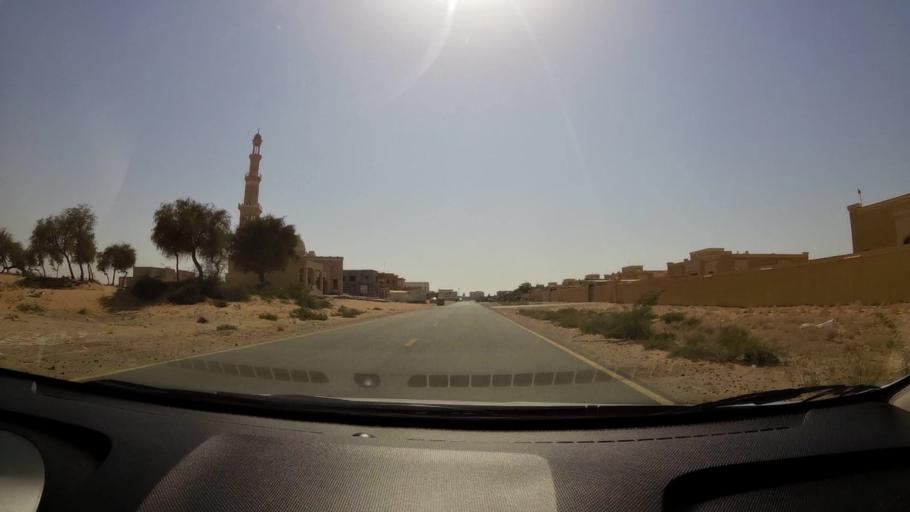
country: AE
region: Umm al Qaywayn
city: Umm al Qaywayn
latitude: 25.4759
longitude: 55.6130
